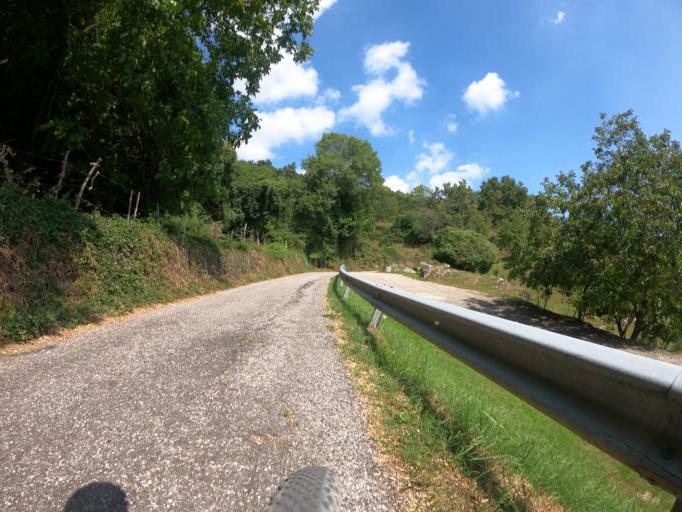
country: IT
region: Veneto
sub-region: Provincia di Verona
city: Dolce
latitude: 45.6313
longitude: 10.8264
